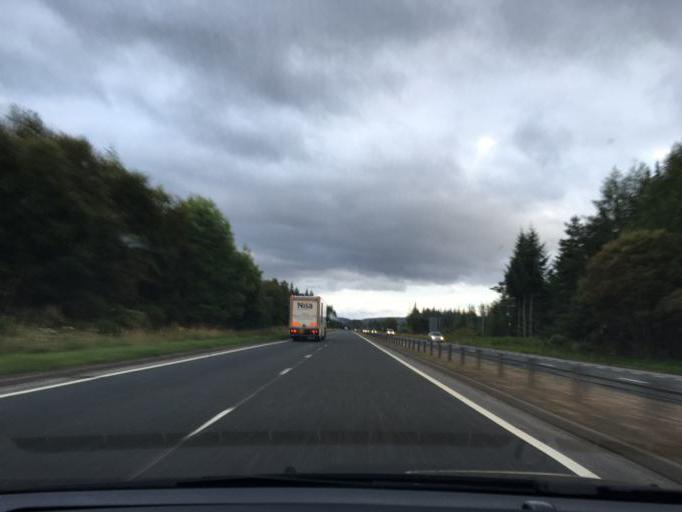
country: GB
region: Scotland
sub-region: Highland
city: Inverness
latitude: 57.4447
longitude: -4.1497
